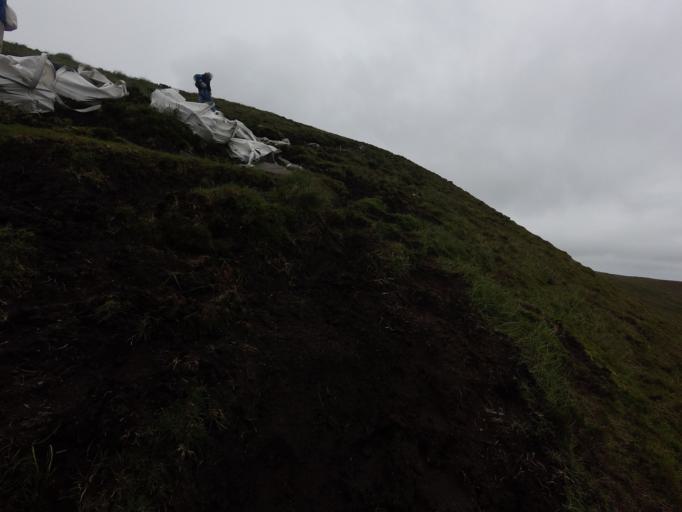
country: IE
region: Ulster
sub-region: County Donegal
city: Killybegs
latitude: 54.6453
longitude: -8.6878
